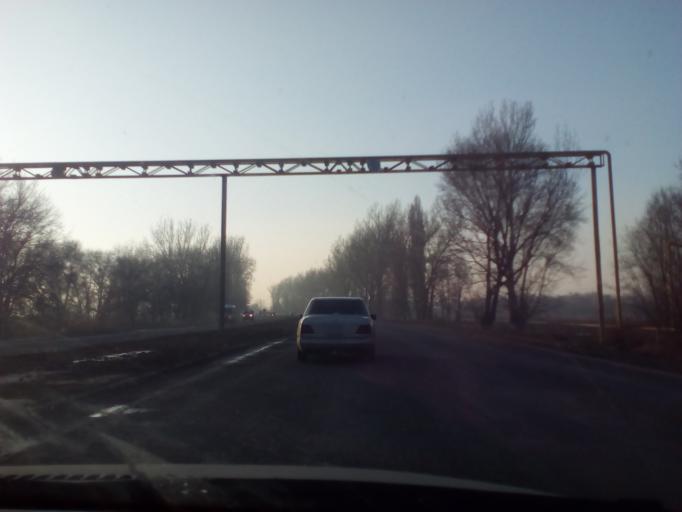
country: KZ
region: Almaty Oblysy
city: Burunday
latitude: 43.2235
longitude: 76.6091
